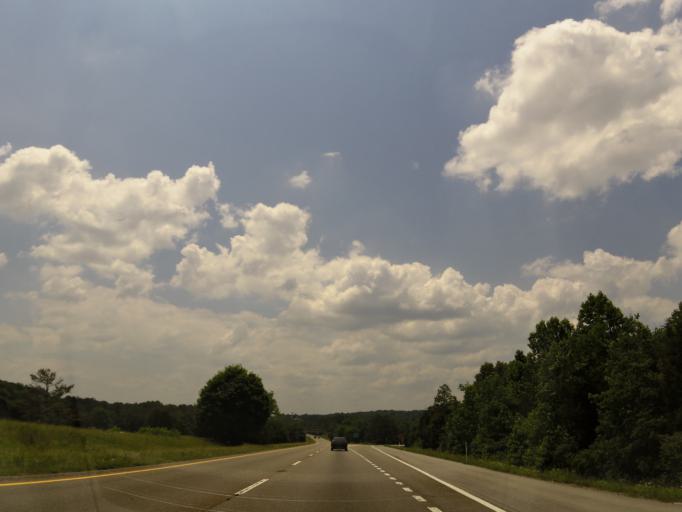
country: US
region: Tennessee
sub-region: Loudon County
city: Loudon
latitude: 35.7871
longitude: -84.3388
